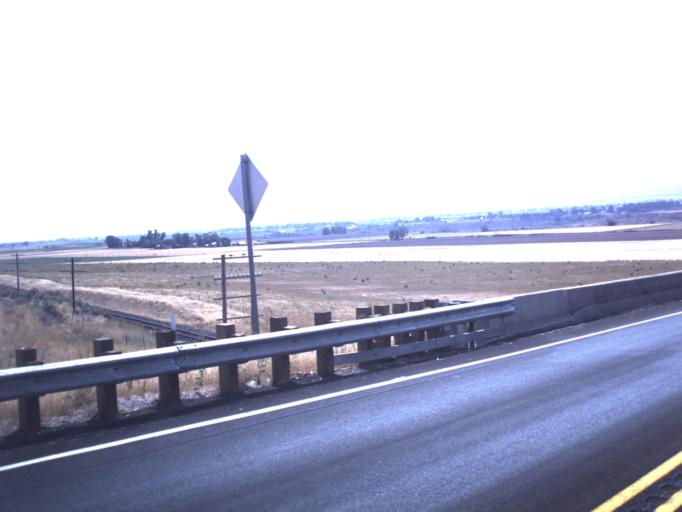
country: US
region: Utah
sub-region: Box Elder County
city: Garland
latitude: 41.7851
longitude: -112.0921
